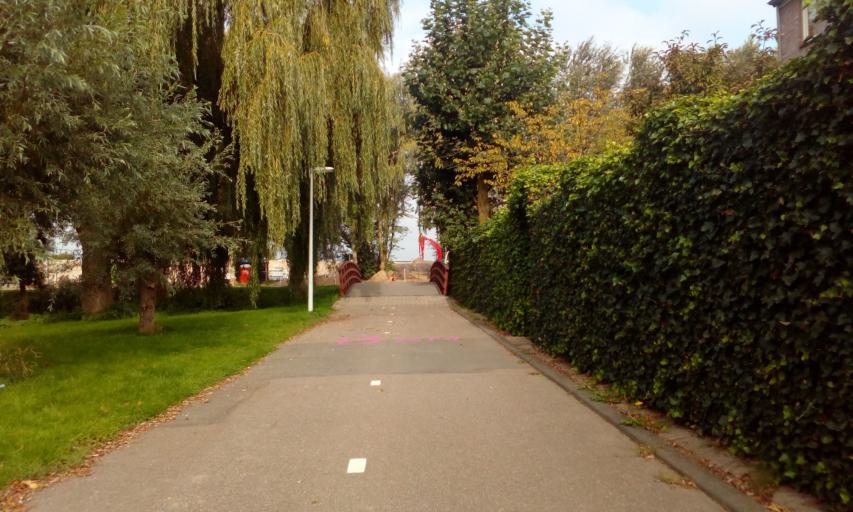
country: NL
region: South Holland
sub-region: Gemeente Voorschoten
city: Voorschoten
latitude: 52.1545
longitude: 4.4441
